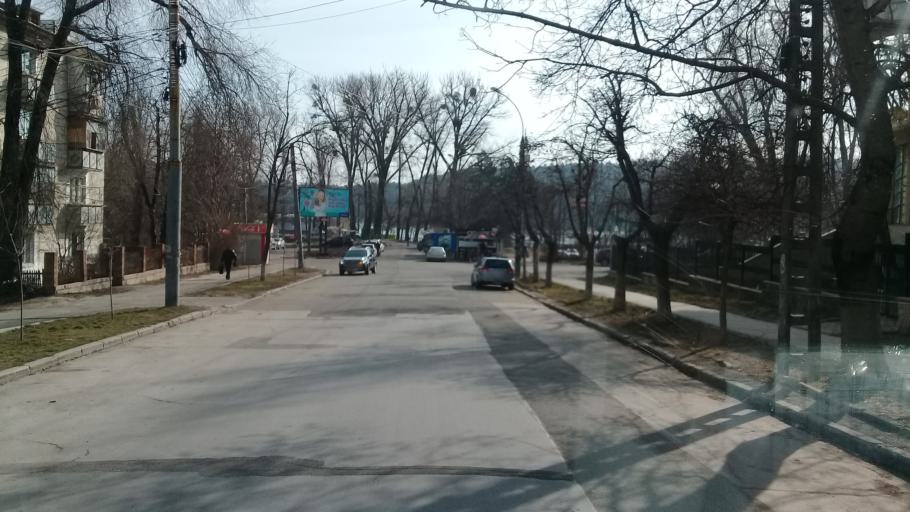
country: MD
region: Chisinau
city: Chisinau
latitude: 47.0204
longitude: 28.8071
